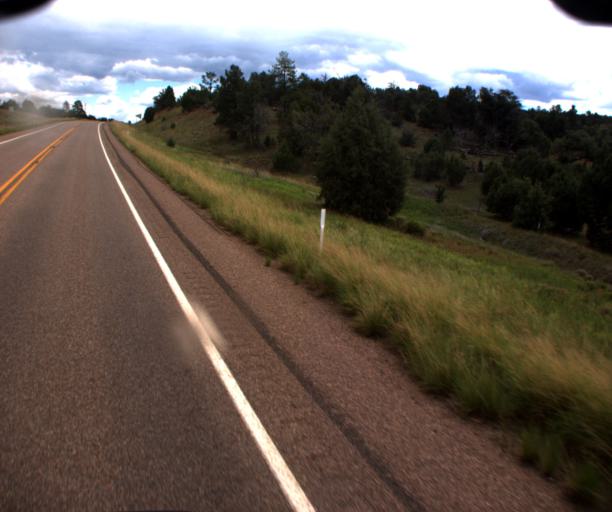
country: US
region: Arizona
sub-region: Navajo County
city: Linden
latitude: 34.3423
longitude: -110.2844
